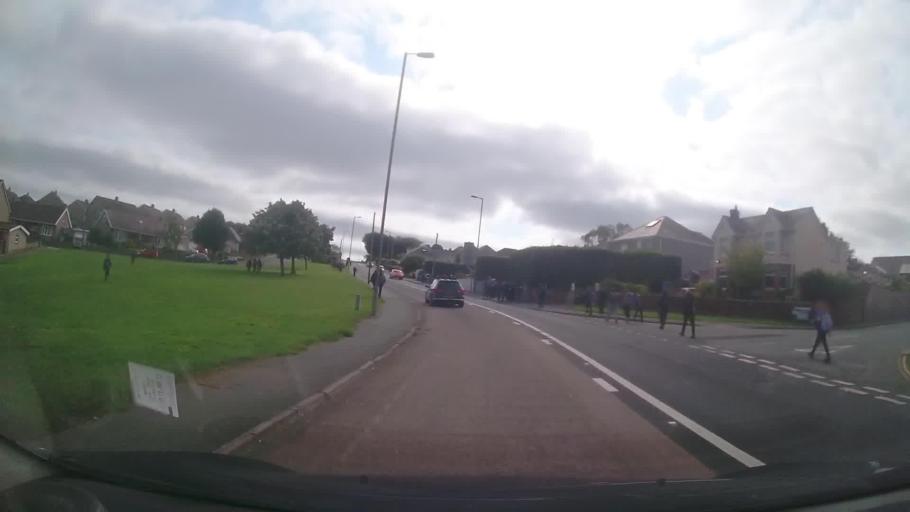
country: GB
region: Wales
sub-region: Pembrokeshire
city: Steynton
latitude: 51.7218
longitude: -5.0238
